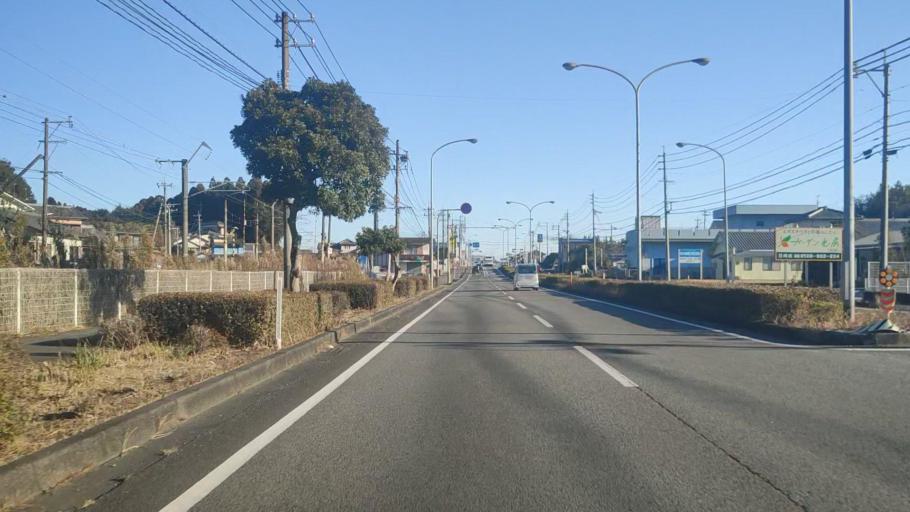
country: JP
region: Miyazaki
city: Nobeoka
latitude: 32.4556
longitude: 131.6437
